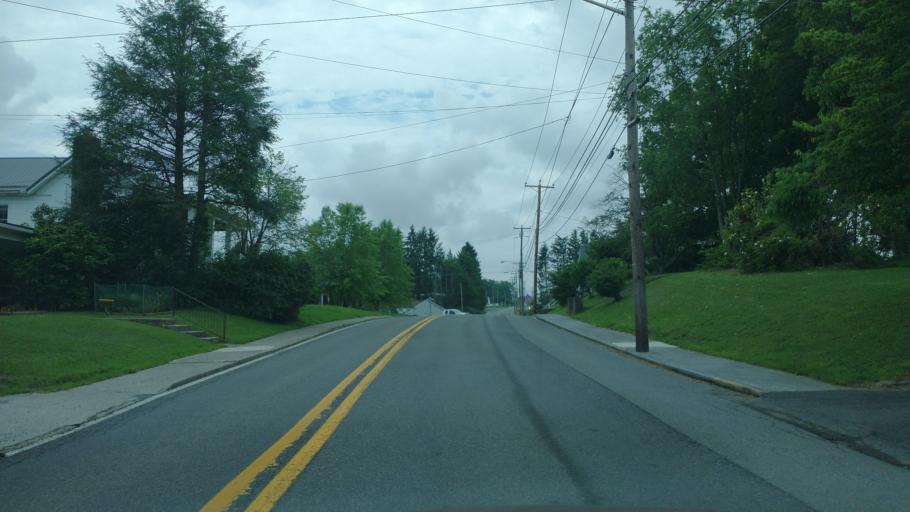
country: US
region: West Virginia
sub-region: Mercer County
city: Athens
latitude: 37.4197
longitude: -81.0156
